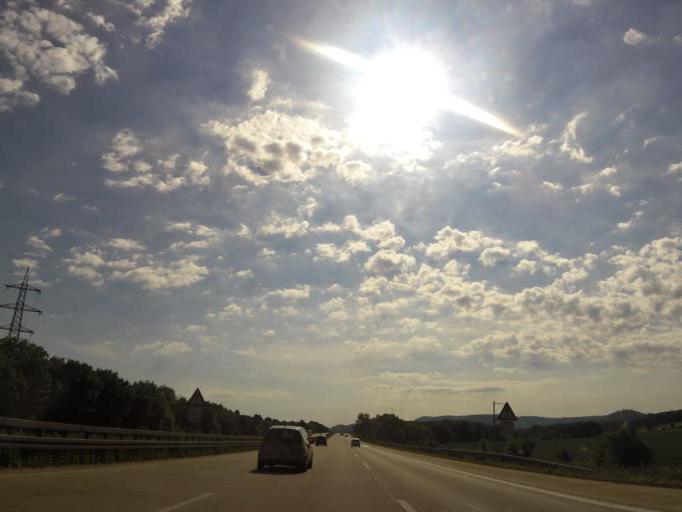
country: DE
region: Baden-Wuerttemberg
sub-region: Regierungsbezirk Stuttgart
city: Kirchheim unter Teck
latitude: 48.6296
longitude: 9.4799
